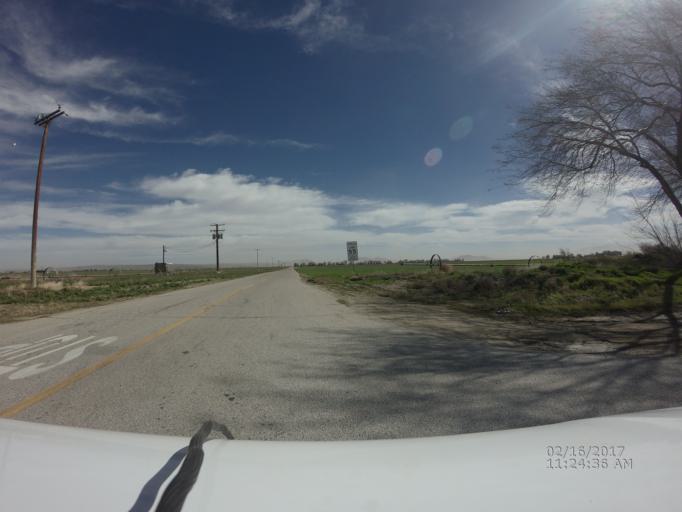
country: US
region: California
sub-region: Los Angeles County
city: Lake Los Angeles
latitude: 34.7047
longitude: -117.9341
